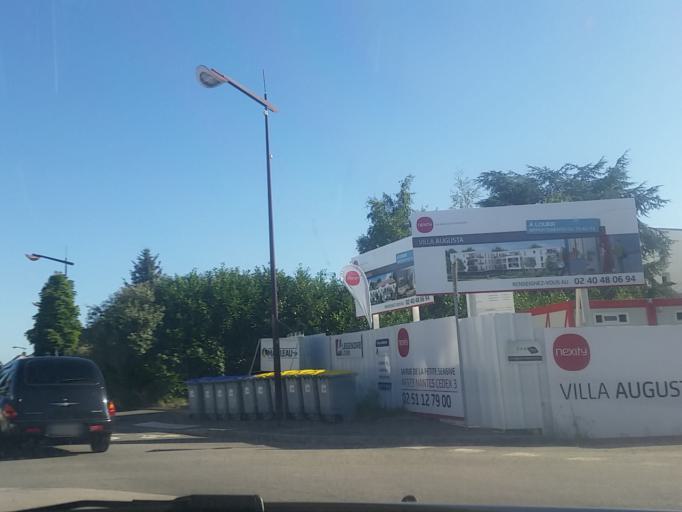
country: FR
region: Pays de la Loire
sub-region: Departement de la Loire-Atlantique
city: Reze
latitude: 47.1759
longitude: -1.5438
